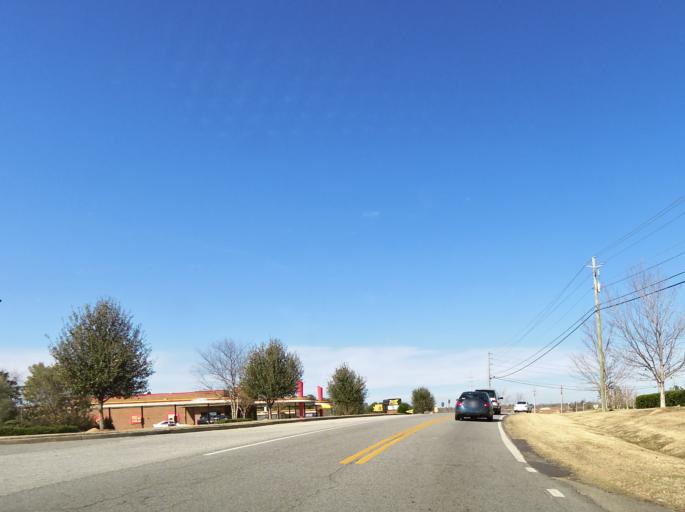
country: US
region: Georgia
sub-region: Bibb County
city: West Point
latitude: 32.8776
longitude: -83.7636
